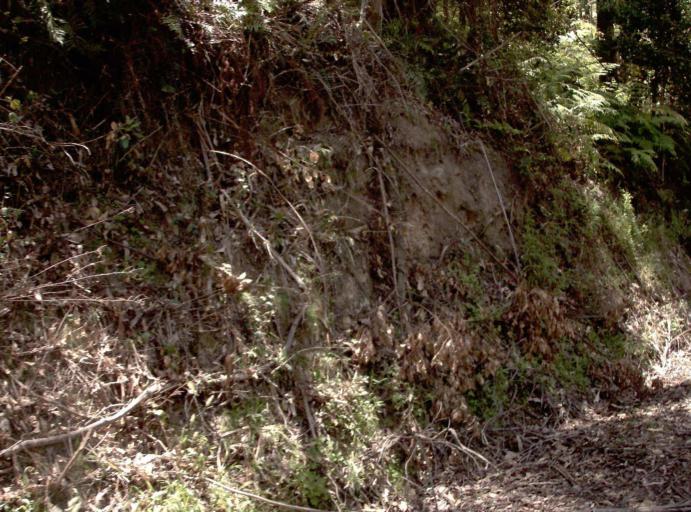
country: AU
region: New South Wales
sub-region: Bombala
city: Bombala
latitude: -37.4650
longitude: 148.9351
